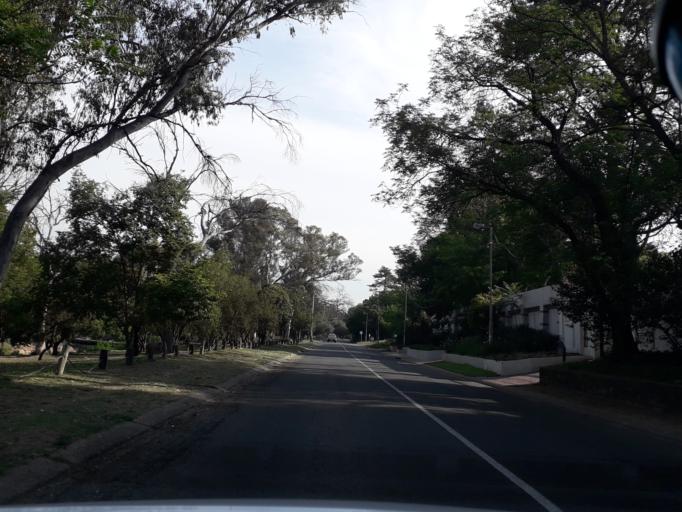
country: ZA
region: Gauteng
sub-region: City of Johannesburg Metropolitan Municipality
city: Midrand
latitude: -26.0645
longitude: 28.0414
